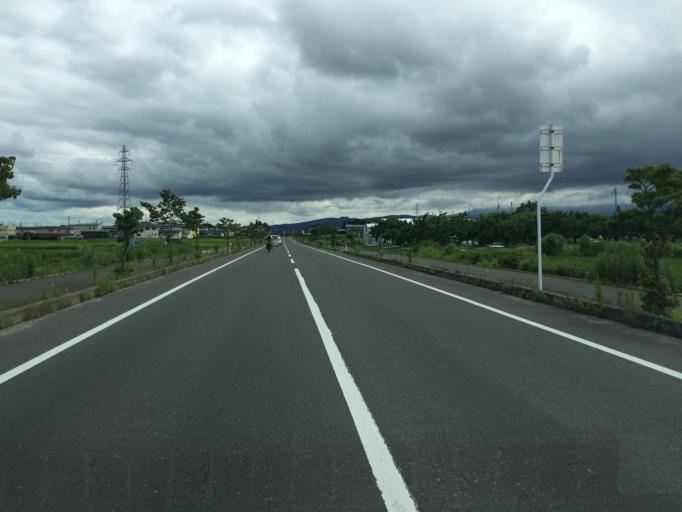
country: JP
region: Fukushima
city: Fukushima-shi
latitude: 37.7944
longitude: 140.4285
